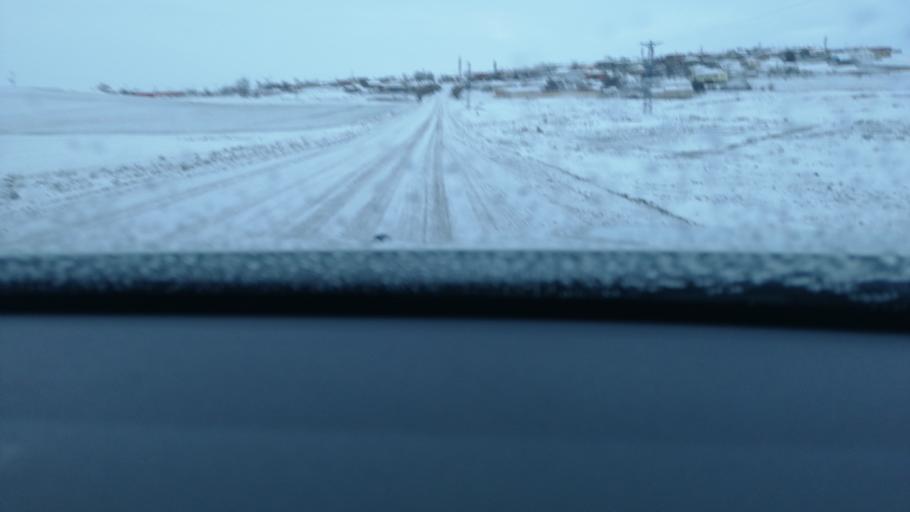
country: TR
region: Aksaray
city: Agacoren
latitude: 38.9399
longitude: 33.9478
